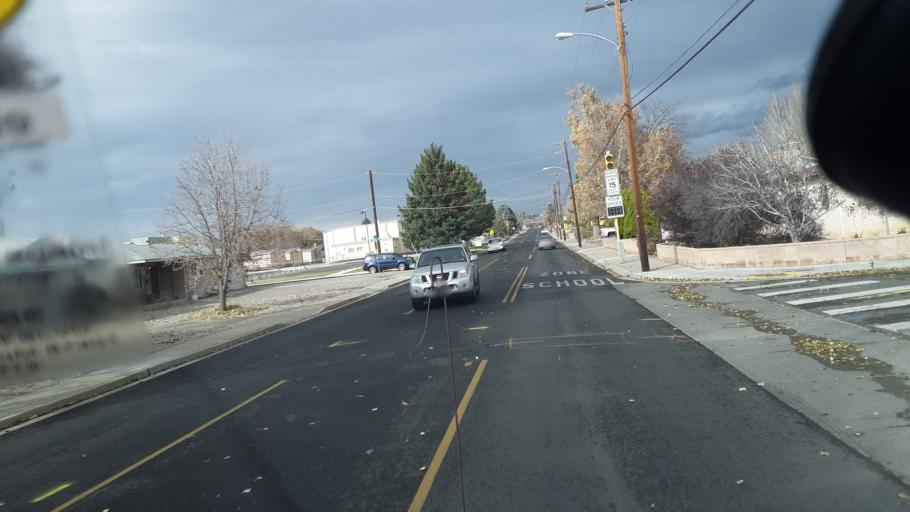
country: US
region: New Mexico
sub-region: San Juan County
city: Farmington
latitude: 36.7424
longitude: -108.1978
